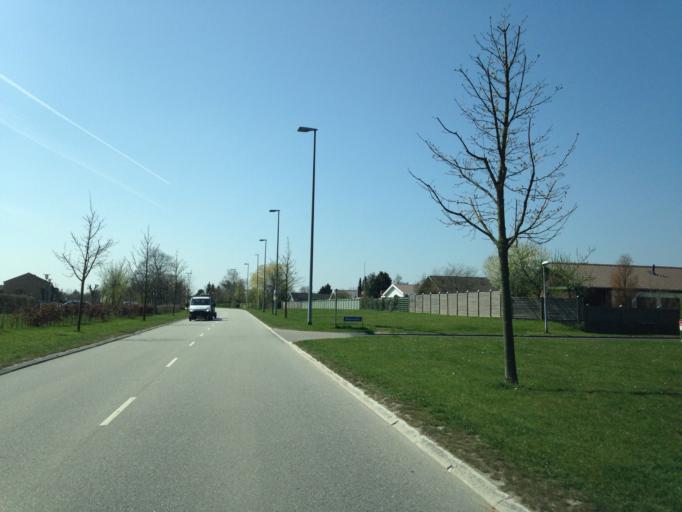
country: DK
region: Zealand
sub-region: Greve Kommune
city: Greve
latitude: 55.5882
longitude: 12.2737
